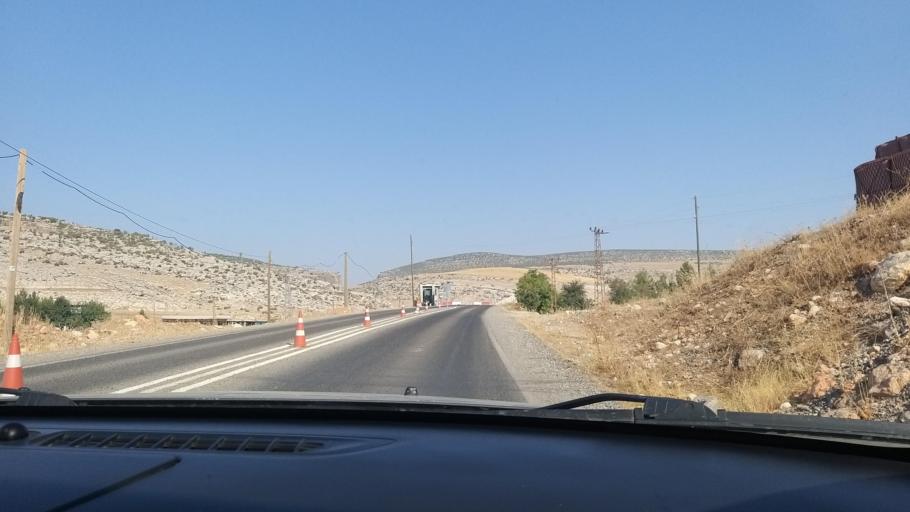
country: TR
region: Diyarbakir
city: Malabadi
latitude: 38.1369
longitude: 41.1937
